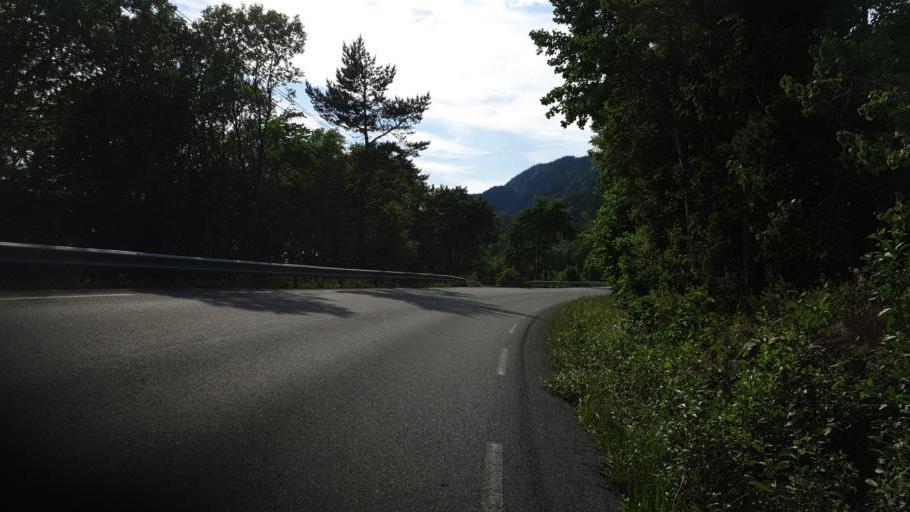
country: NO
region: Sor-Trondelag
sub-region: Trondheim
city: Trondheim
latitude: 63.5562
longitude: 10.3050
